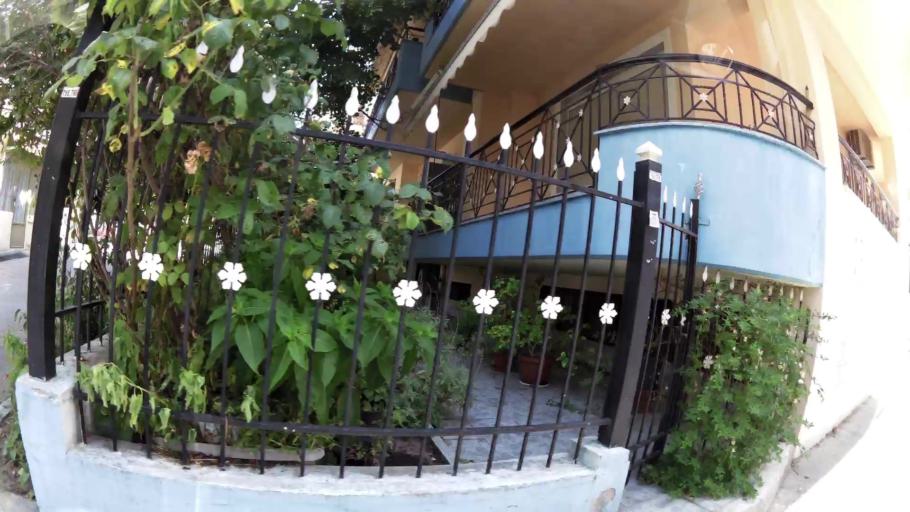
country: GR
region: Central Macedonia
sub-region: Nomos Thessalonikis
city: Evosmos
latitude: 40.6746
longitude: 22.9120
